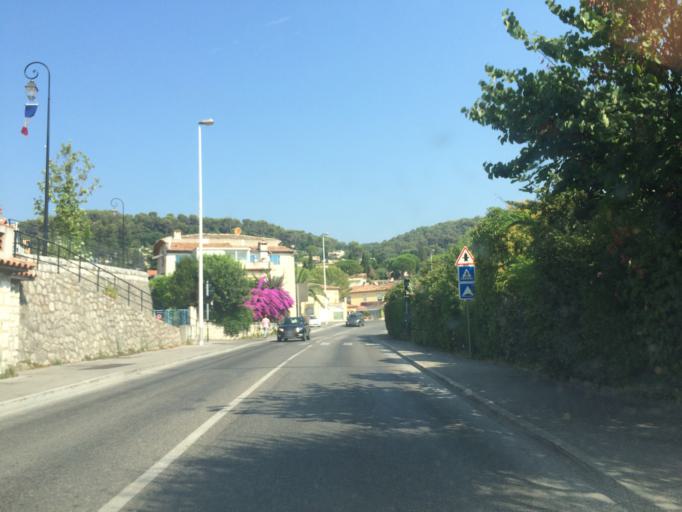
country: FR
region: Provence-Alpes-Cote d'Azur
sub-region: Departement des Alpes-Maritimes
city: La Colle-sur-Loup
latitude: 43.6882
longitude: 7.1049
